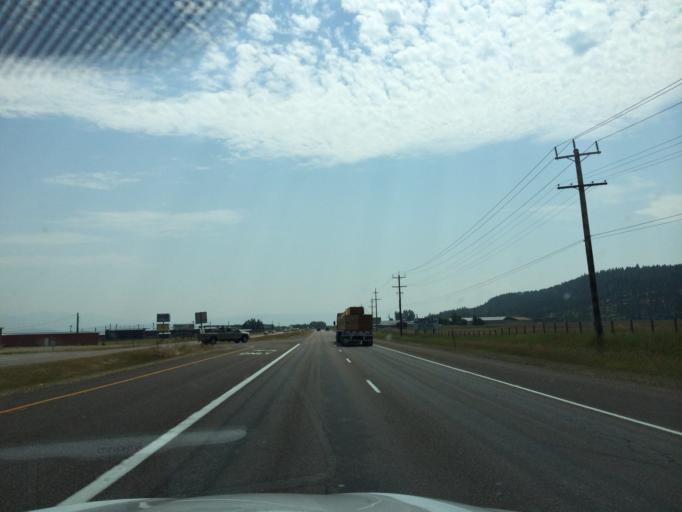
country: US
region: Montana
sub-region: Flathead County
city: Kalispell
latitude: 48.1353
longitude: -114.2733
